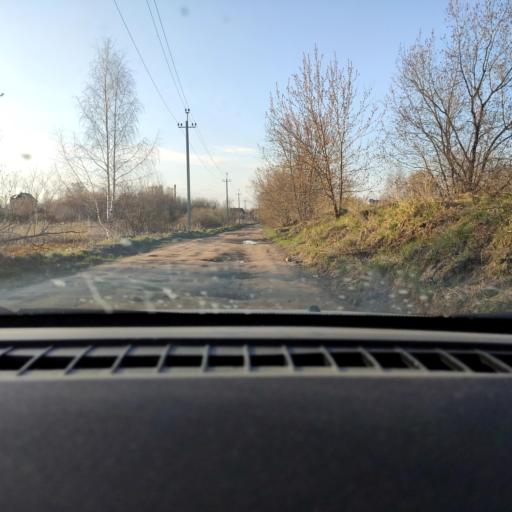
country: RU
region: Perm
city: Perm
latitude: 58.0247
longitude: 56.2107
